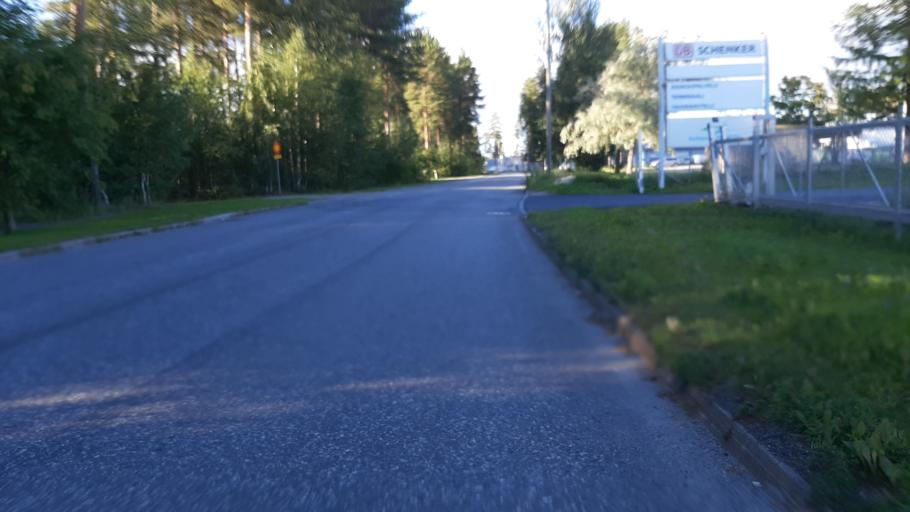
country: FI
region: North Karelia
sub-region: Joensuu
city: Joensuu
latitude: 62.6244
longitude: 29.7708
